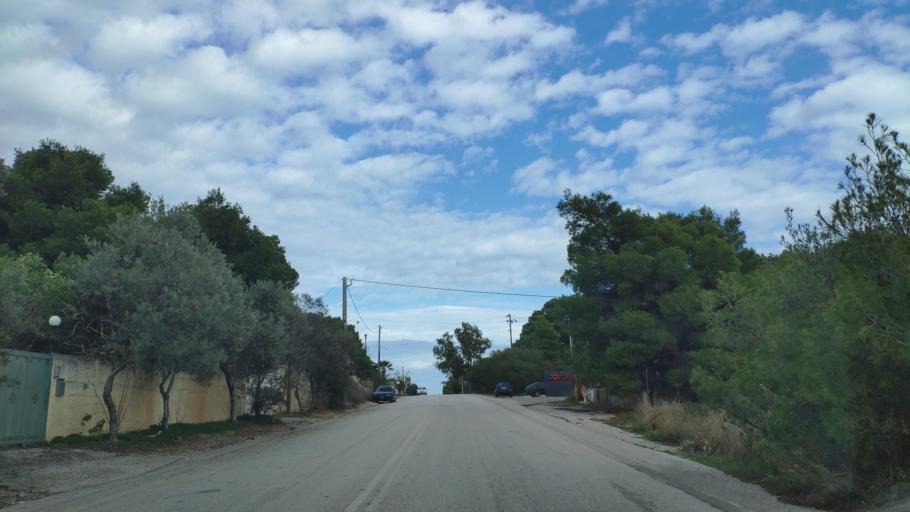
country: GR
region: Attica
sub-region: Nomarchia Anatolikis Attikis
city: Artemida
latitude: 37.9302
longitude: 24.0046
